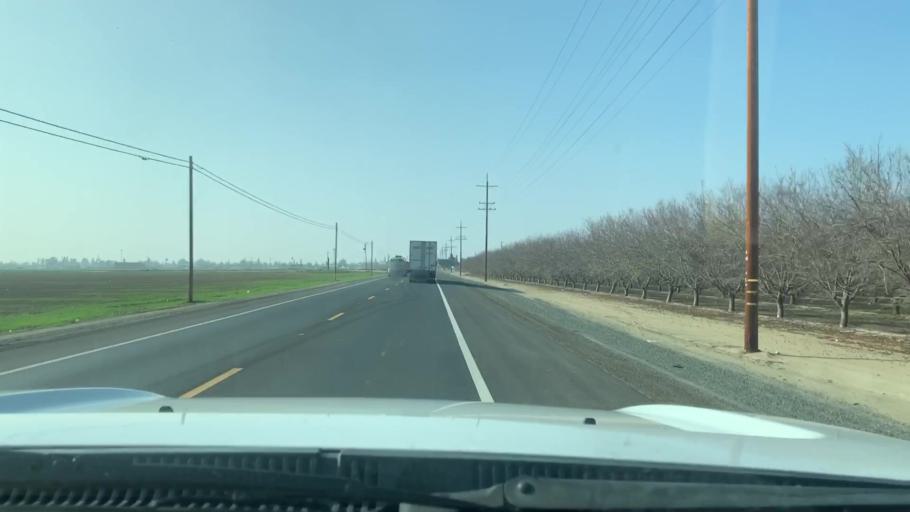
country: US
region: California
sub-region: Kern County
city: Wasco
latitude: 35.6016
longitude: -119.3181
